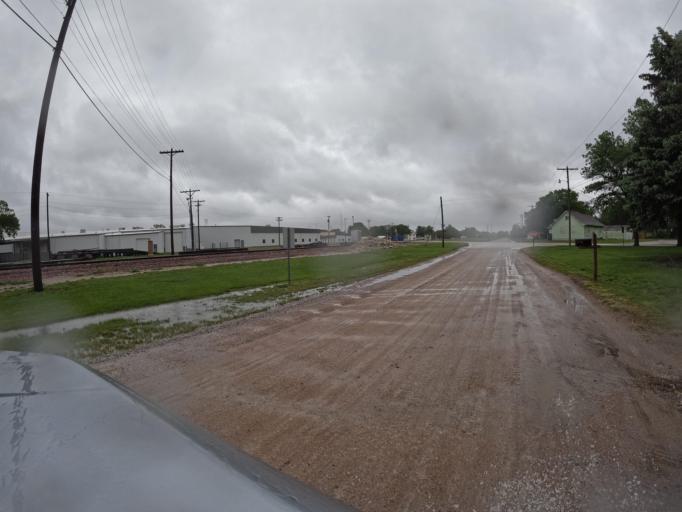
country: US
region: Nebraska
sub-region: Saline County
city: Wilber
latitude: 40.3942
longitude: -96.9166
